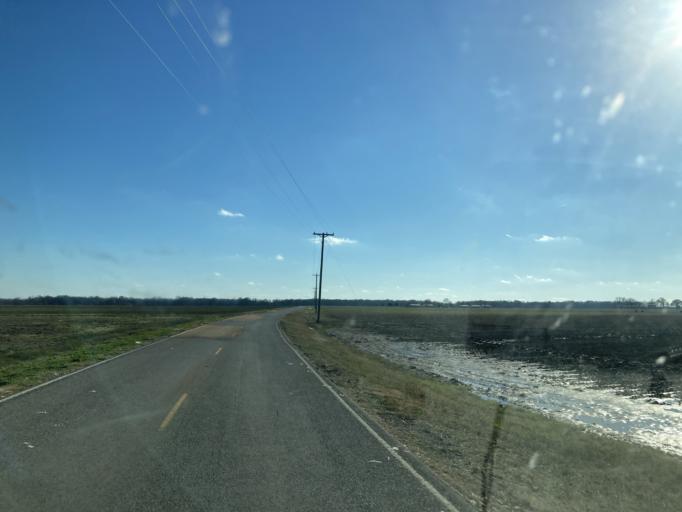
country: US
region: Mississippi
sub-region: Yazoo County
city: Yazoo City
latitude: 32.9321
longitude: -90.5059
